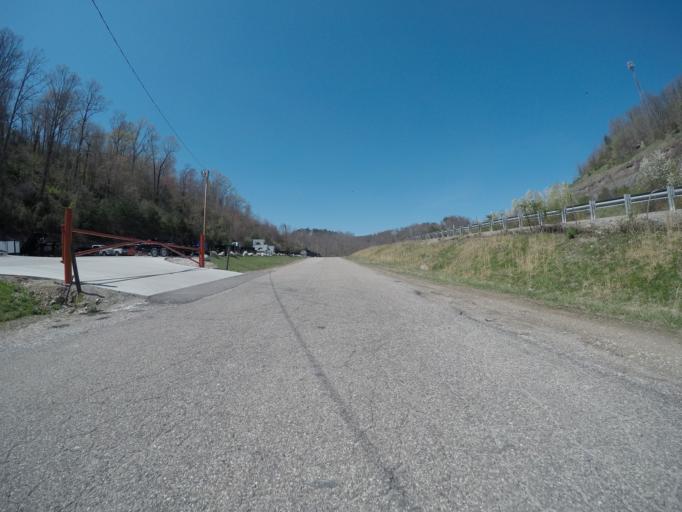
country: US
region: West Virginia
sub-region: Kanawha County
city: Charleston
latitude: 38.3940
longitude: -81.5915
